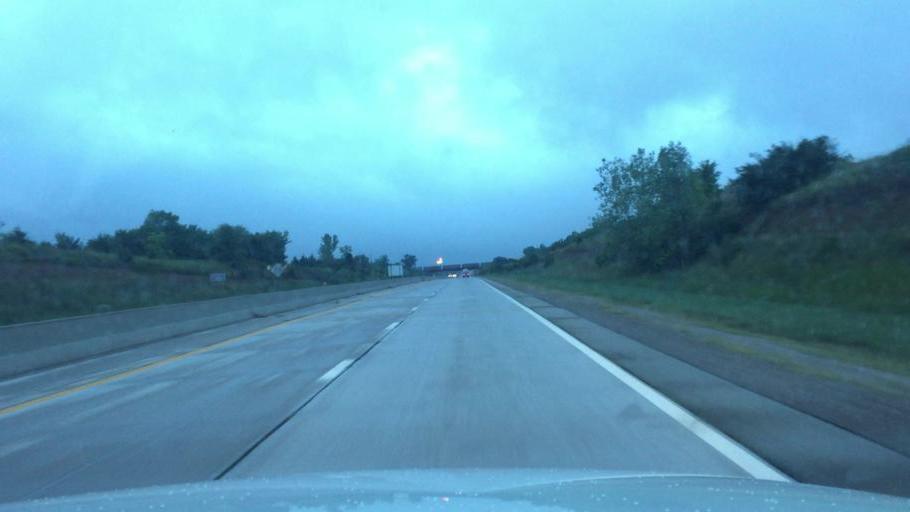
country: US
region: Kansas
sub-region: Neosho County
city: Chanute
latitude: 37.6693
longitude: -95.4796
